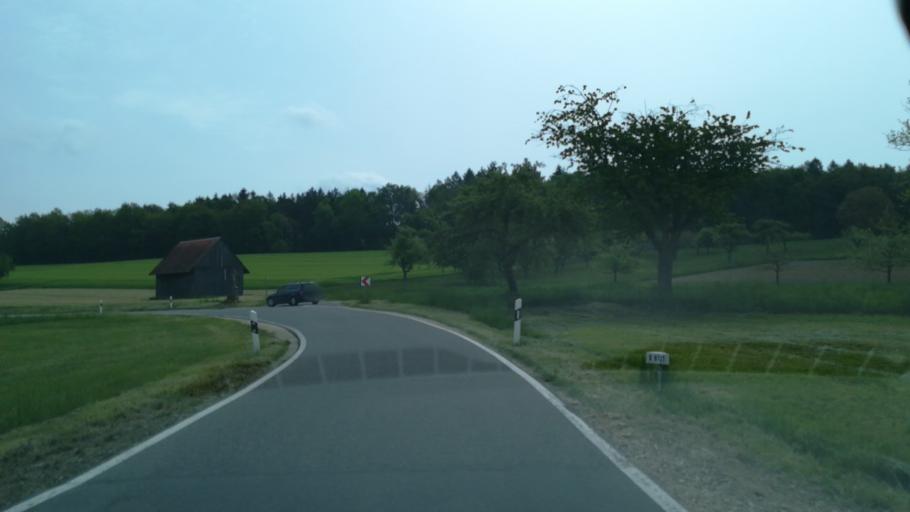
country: DE
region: Baden-Wuerttemberg
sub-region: Freiburg Region
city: Volkertshausen
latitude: 47.7989
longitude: 8.8830
